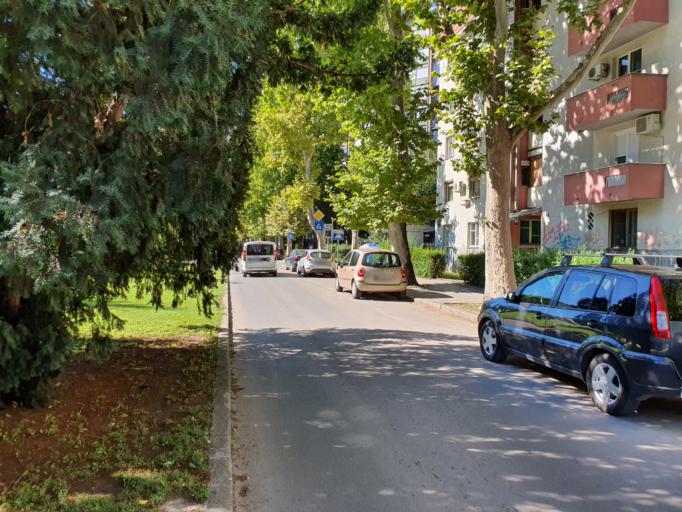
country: RS
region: Autonomna Pokrajina Vojvodina
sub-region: Severnobacki Okrug
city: Subotica
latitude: 46.1042
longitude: 19.6603
